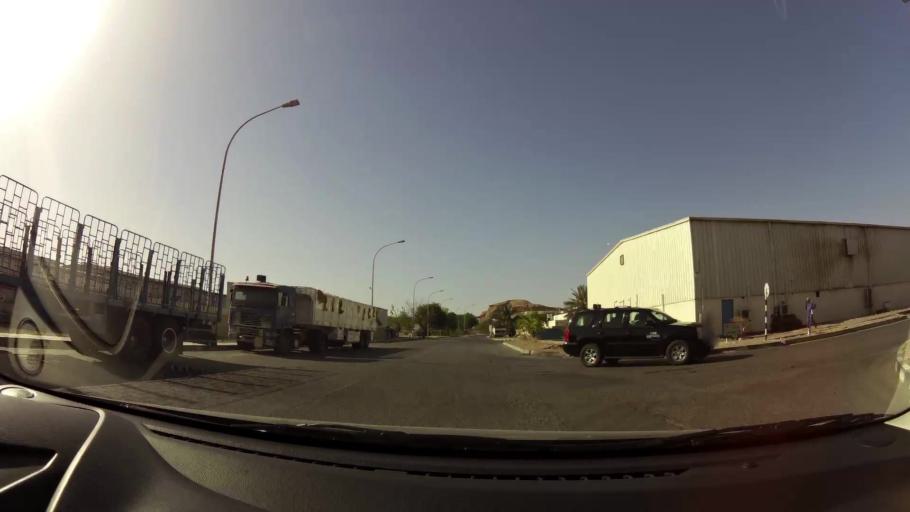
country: OM
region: Muhafazat Masqat
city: As Sib al Jadidah
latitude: 23.5558
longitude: 58.2074
